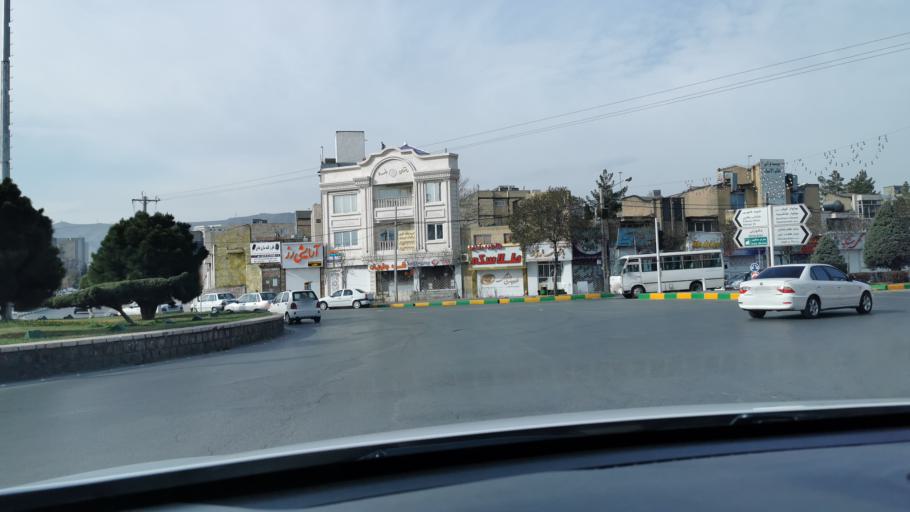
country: IR
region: Razavi Khorasan
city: Mashhad
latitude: 36.3051
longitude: 59.5127
